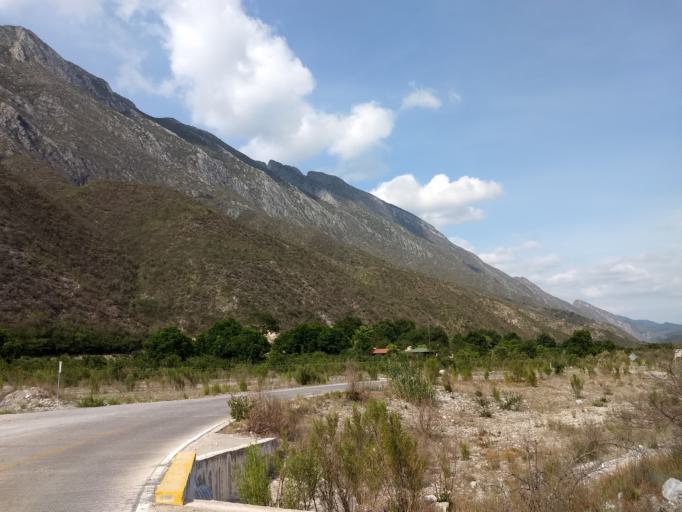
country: MX
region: Nuevo Leon
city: Santiago
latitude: 25.3976
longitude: -100.2973
